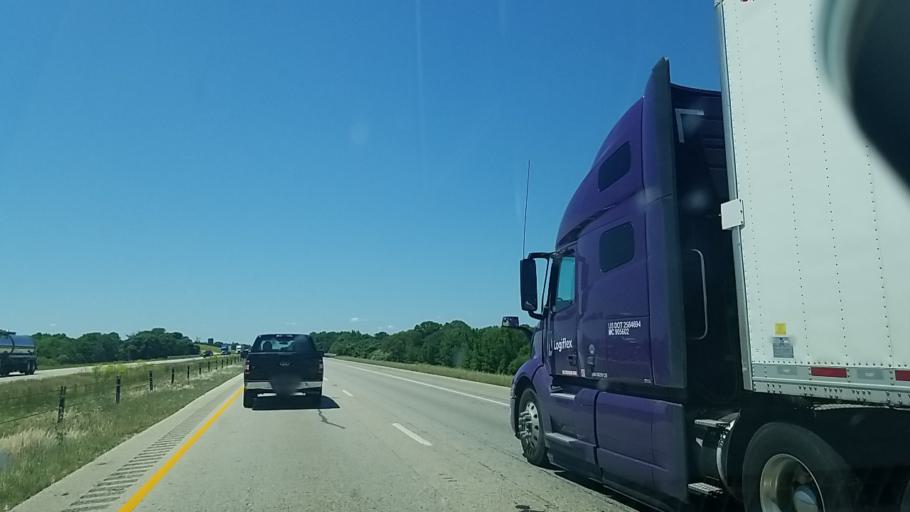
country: US
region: Texas
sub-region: Leon County
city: Buffalo
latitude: 31.4306
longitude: -96.0575
